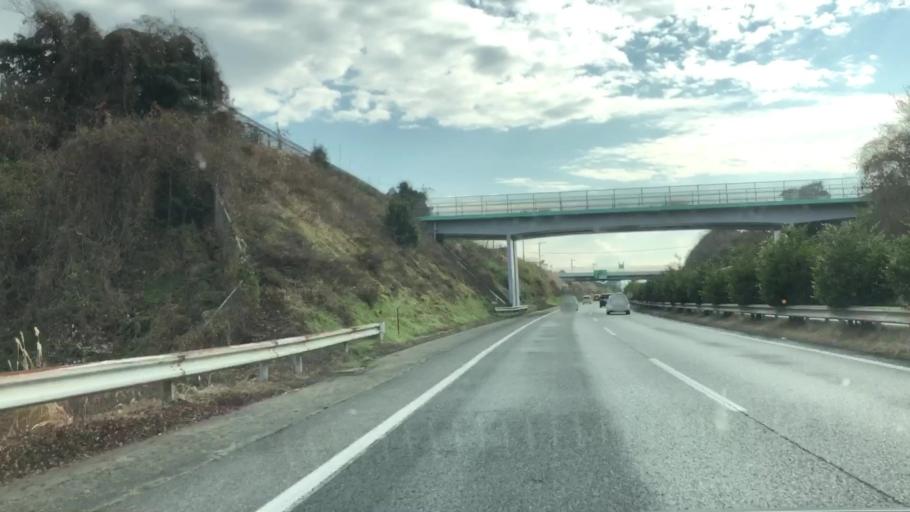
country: JP
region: Fukuoka
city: Setakamachi-takayanagi
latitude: 33.1339
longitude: 130.5167
